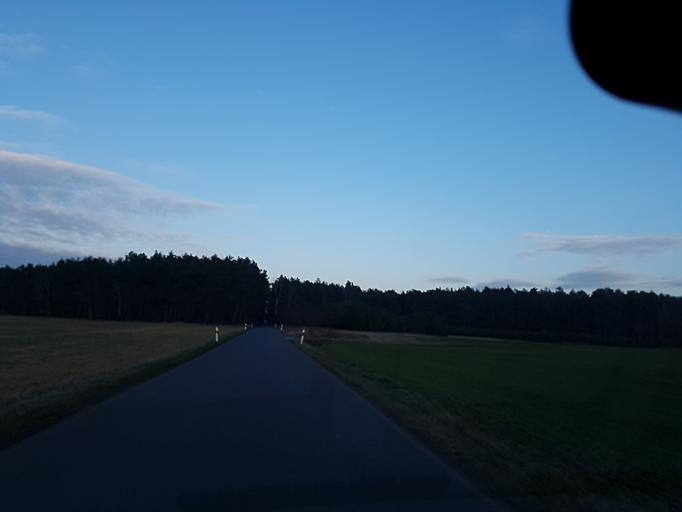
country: DE
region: Brandenburg
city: Ruckersdorf
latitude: 51.5836
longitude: 13.5848
